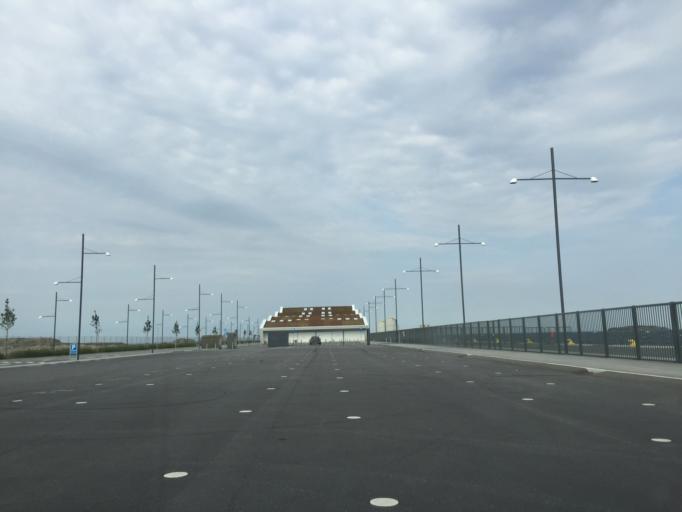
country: DK
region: Capital Region
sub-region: Gentofte Kommune
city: Charlottenlund
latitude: 55.7159
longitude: 12.6249
